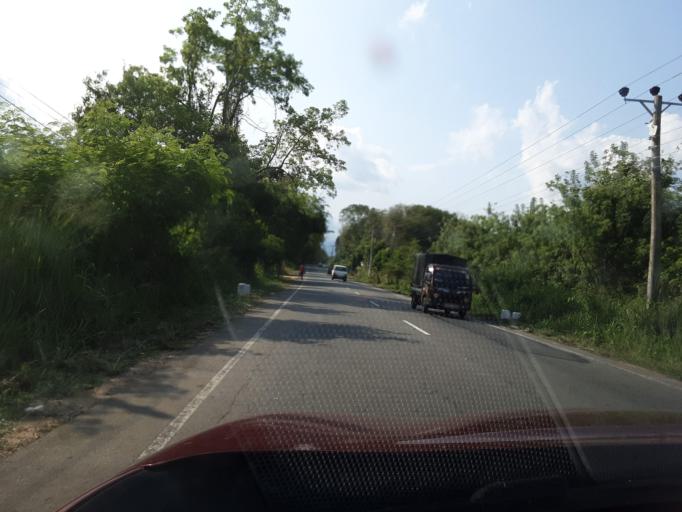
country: LK
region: Uva
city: Haputale
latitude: 6.6036
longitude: 81.1377
